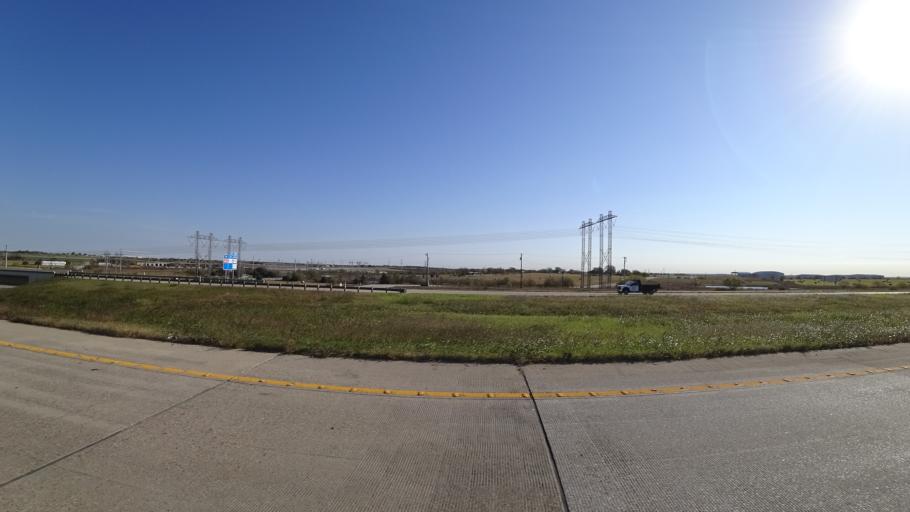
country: US
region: Texas
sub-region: Travis County
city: Pflugerville
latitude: 30.4046
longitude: -97.5834
